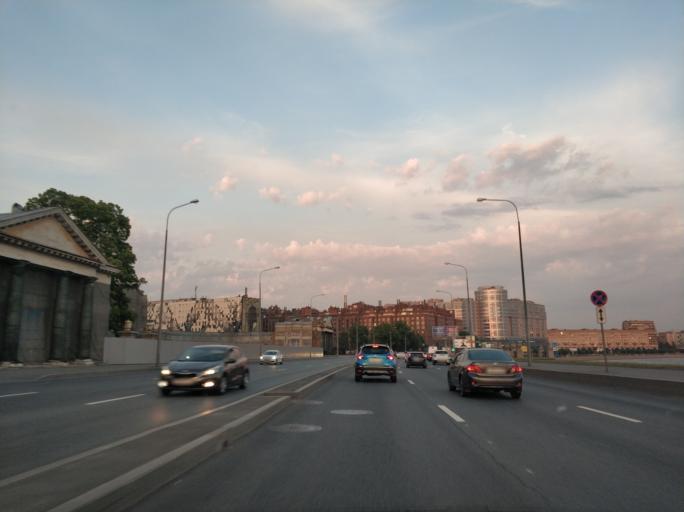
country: RU
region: Leningrad
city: Finlyandskiy
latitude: 59.9588
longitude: 30.3984
